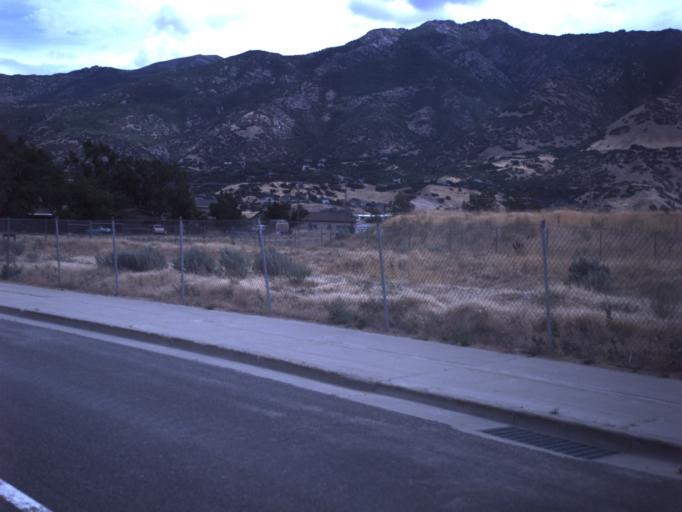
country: US
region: Utah
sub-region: Davis County
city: South Weber
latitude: 41.1305
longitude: -111.9239
